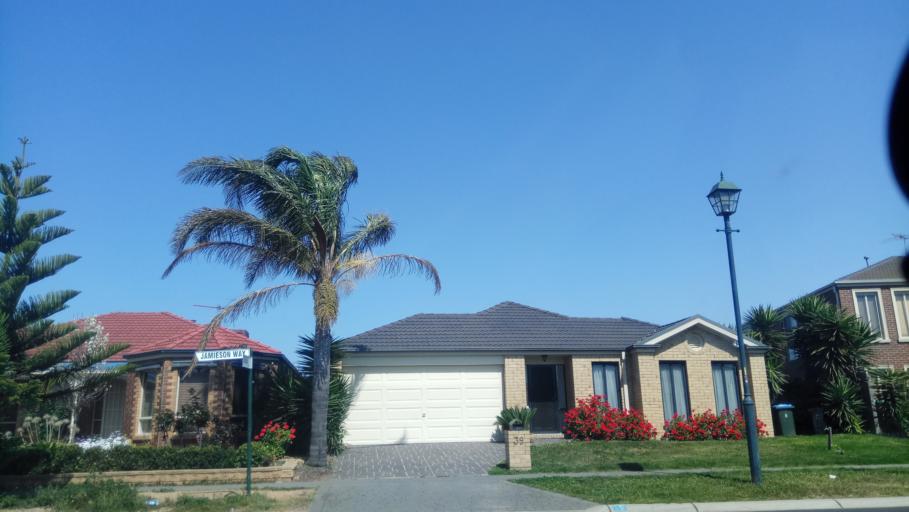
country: AU
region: Victoria
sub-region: Wyndham
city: Point Cook
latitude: -37.8966
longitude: 144.7501
